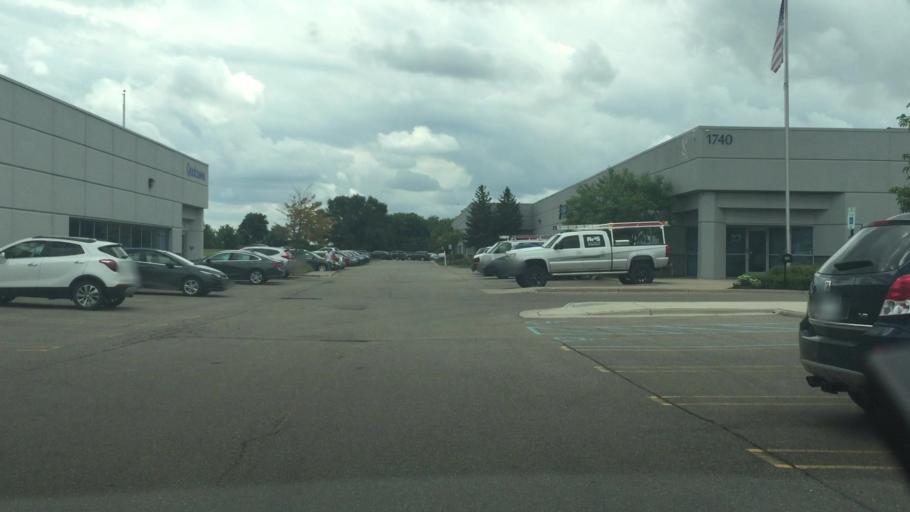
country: US
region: Michigan
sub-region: Oakland County
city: Auburn Hills
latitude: 42.6694
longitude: -83.2431
